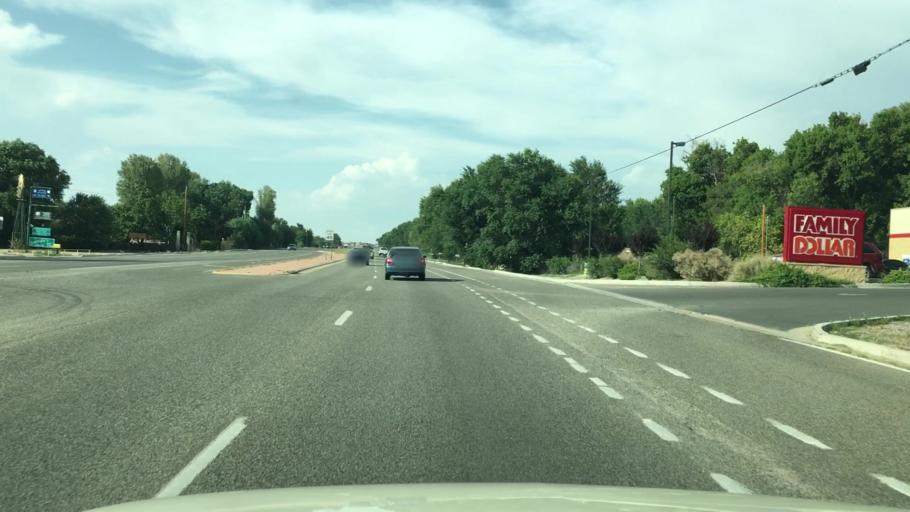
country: US
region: New Mexico
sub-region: Santa Fe County
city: Pojoaque
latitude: 35.8988
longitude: -106.0205
